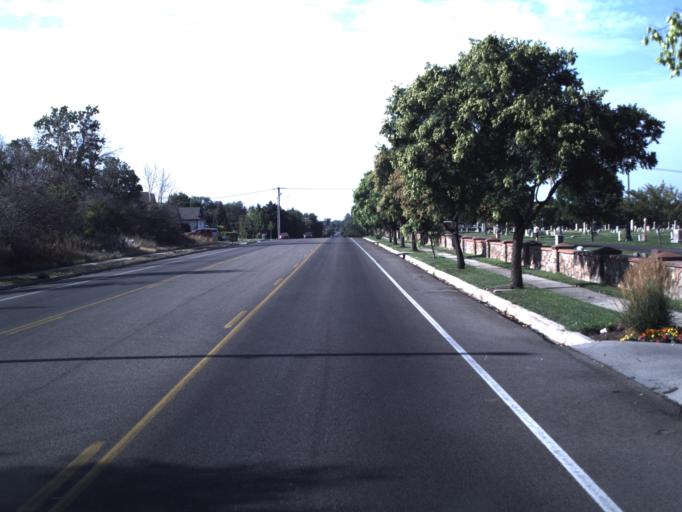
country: US
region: Utah
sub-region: Utah County
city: American Fork
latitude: 40.3910
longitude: -111.7958
